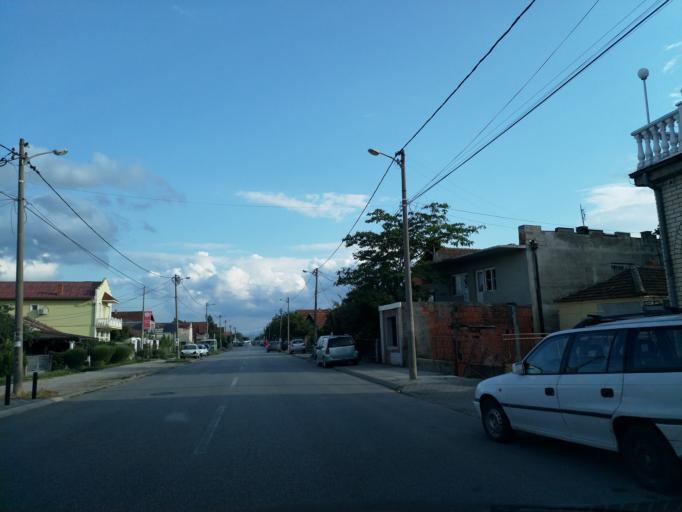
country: RS
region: Central Serbia
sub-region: Pomoravski Okrug
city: Paracin
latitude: 43.8506
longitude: 21.4134
